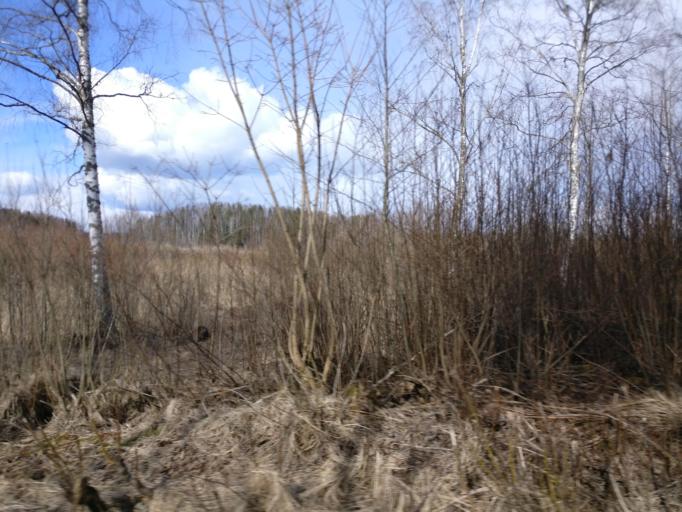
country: FI
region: Varsinais-Suomi
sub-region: Salo
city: Suomusjaervi
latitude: 60.3368
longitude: 23.7000
